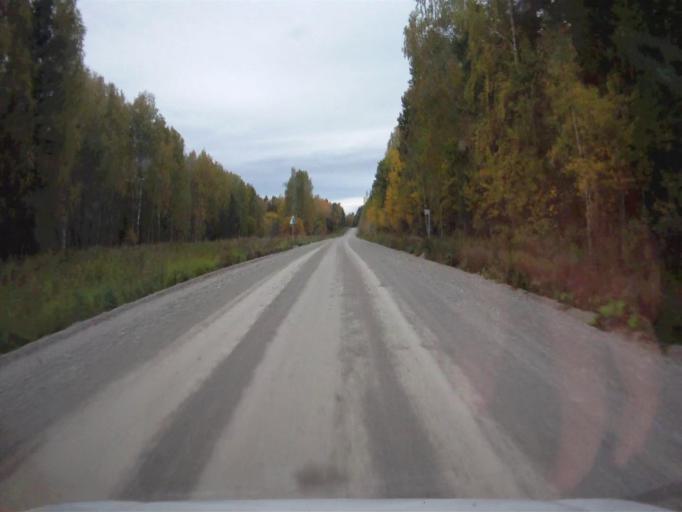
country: RU
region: Chelyabinsk
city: Nyazepetrovsk
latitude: 56.0800
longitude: 59.4233
